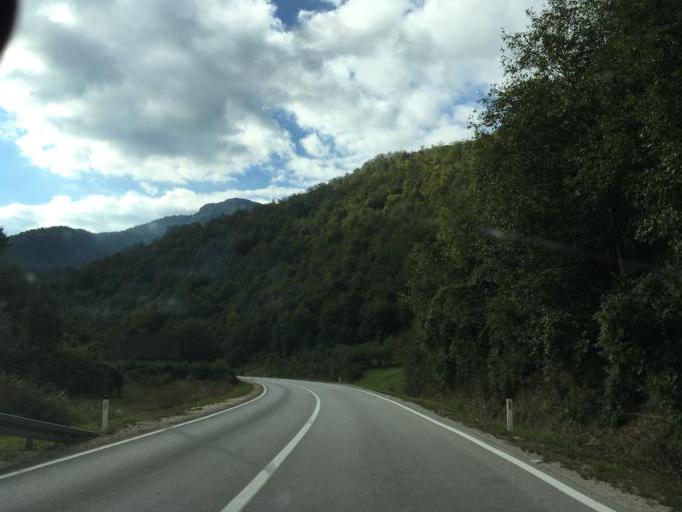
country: BA
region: Federation of Bosnia and Herzegovina
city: Bugojno
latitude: 44.0936
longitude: 17.5641
